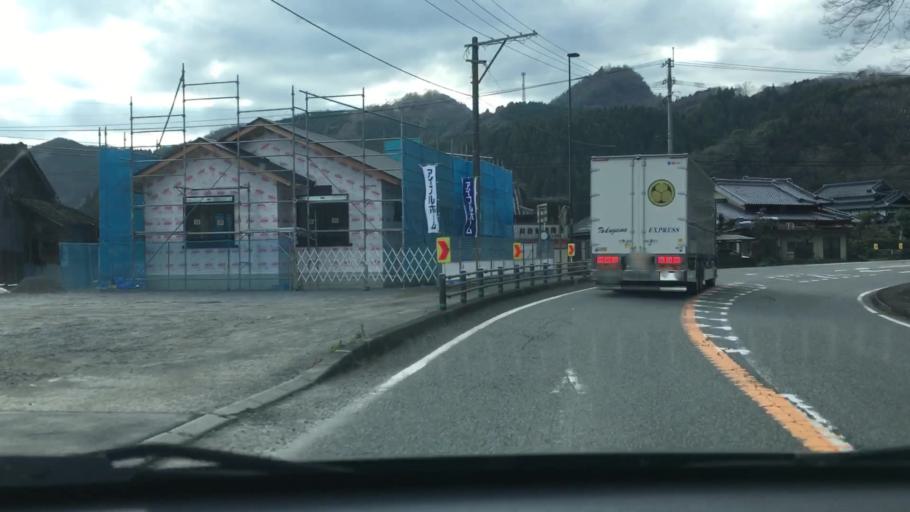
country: JP
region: Oita
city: Usuki
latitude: 33.0072
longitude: 131.7099
